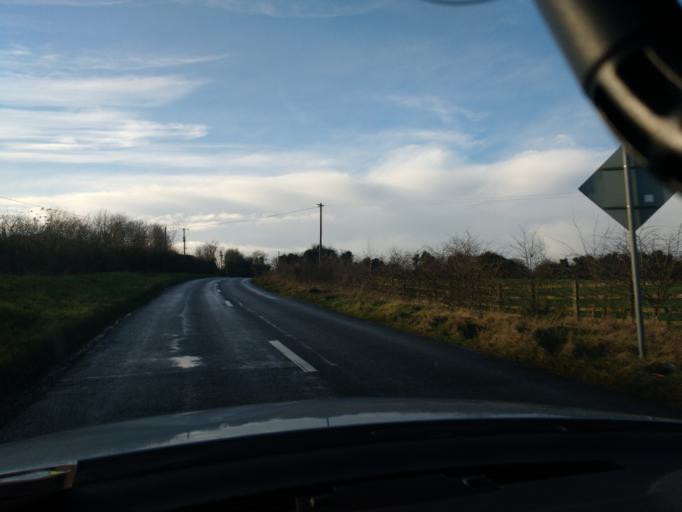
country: IE
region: Munster
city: Thurles
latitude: 52.6323
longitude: -7.7686
